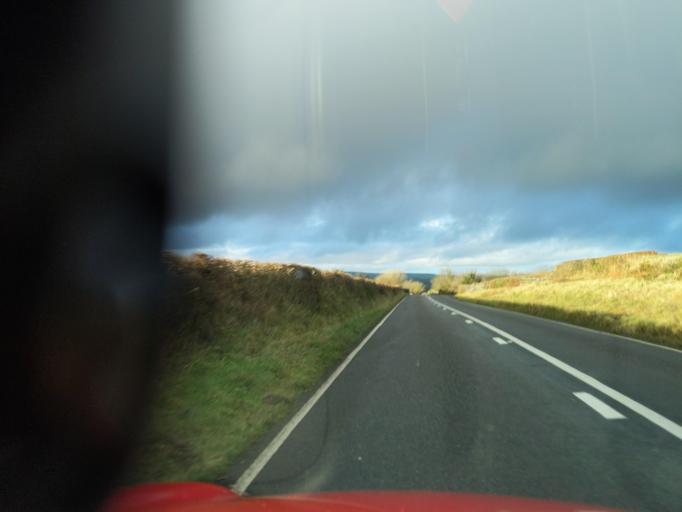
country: GB
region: England
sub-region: Devon
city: Okehampton
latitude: 50.6681
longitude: -4.0876
